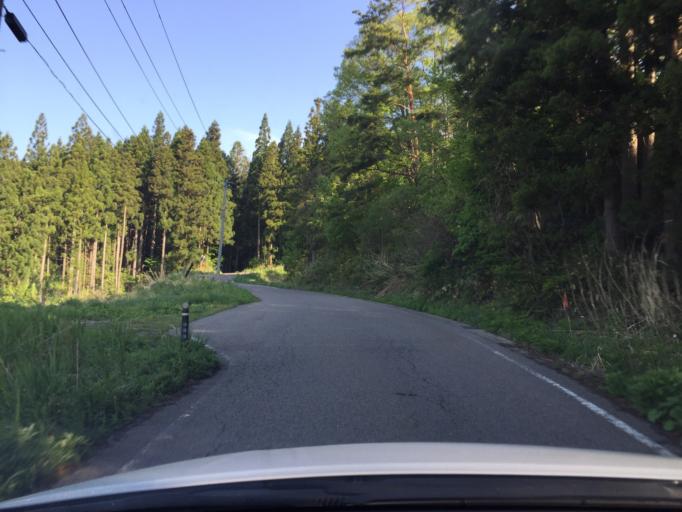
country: JP
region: Fukushima
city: Kitakata
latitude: 37.6714
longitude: 139.8058
